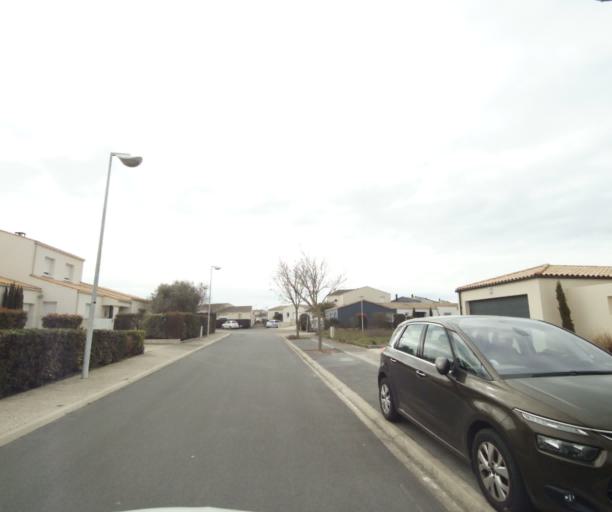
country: FR
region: Poitou-Charentes
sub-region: Departement de la Charente-Maritime
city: Lagord
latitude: 46.1866
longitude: -1.1621
